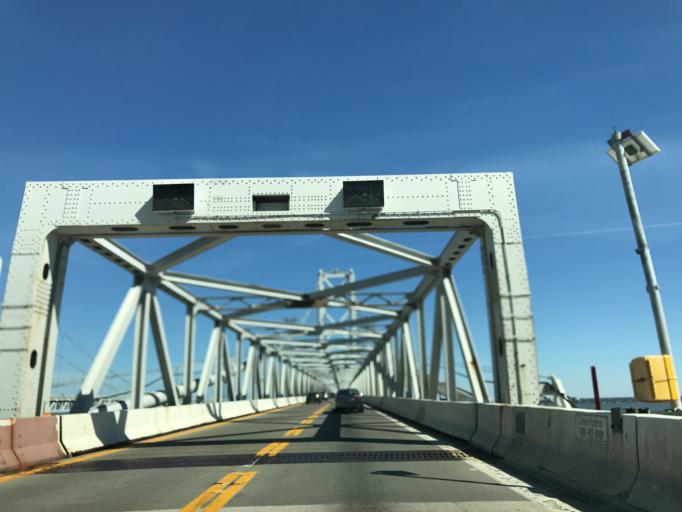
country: US
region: Maryland
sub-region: Queen Anne's County
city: Stevensville
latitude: 38.9942
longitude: -76.3865
